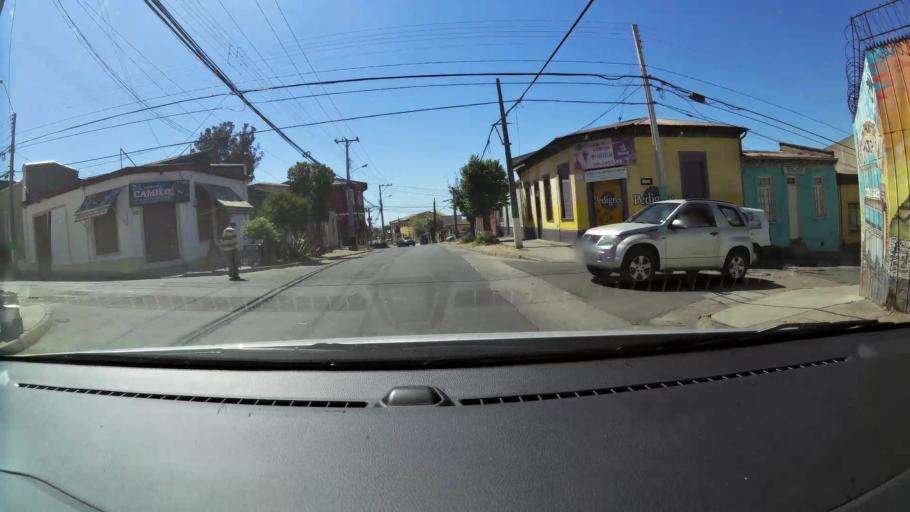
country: CL
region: Valparaiso
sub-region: Provincia de Valparaiso
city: Valparaiso
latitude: -33.0330
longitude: -71.6411
